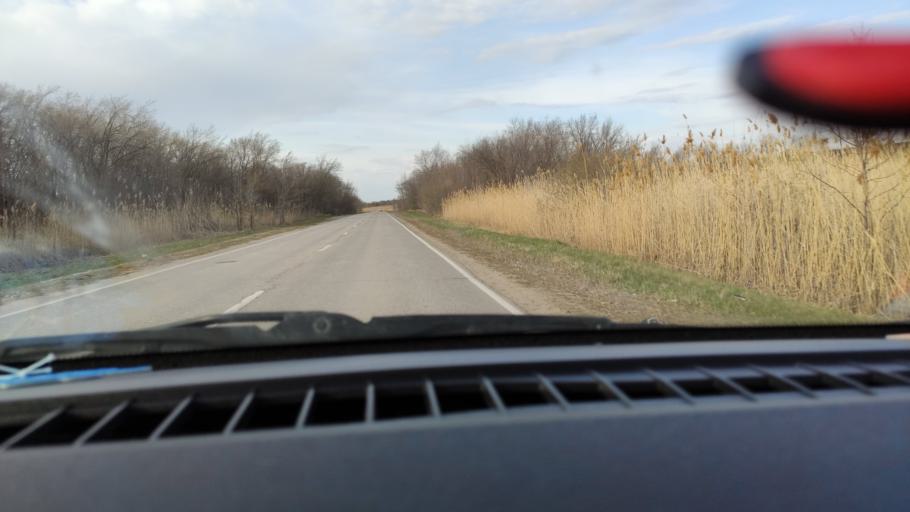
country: RU
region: Saratov
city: Privolzhskiy
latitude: 51.2618
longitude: 45.9456
